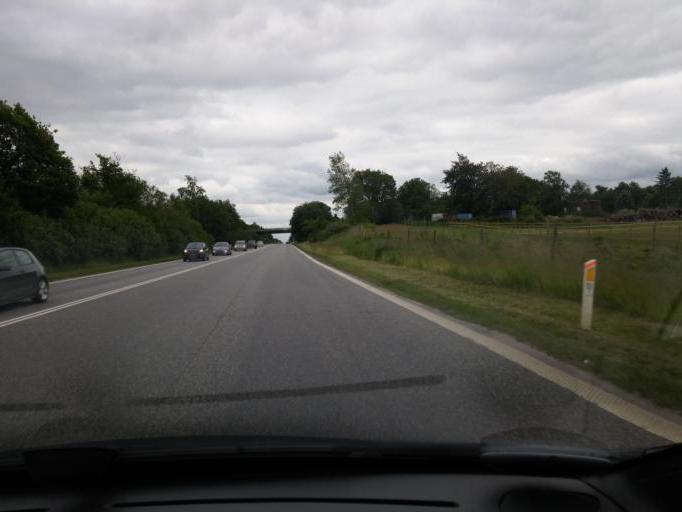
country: DK
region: Capital Region
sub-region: Hillerod Kommune
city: Hillerod
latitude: 55.9304
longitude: 12.2515
